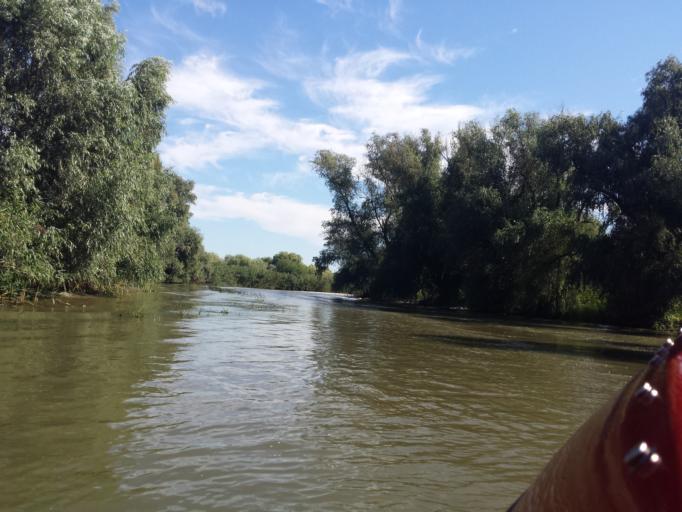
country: RO
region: Tulcea
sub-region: Comuna Mahmudia
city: Mahmudia
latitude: 45.2374
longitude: 29.1148
